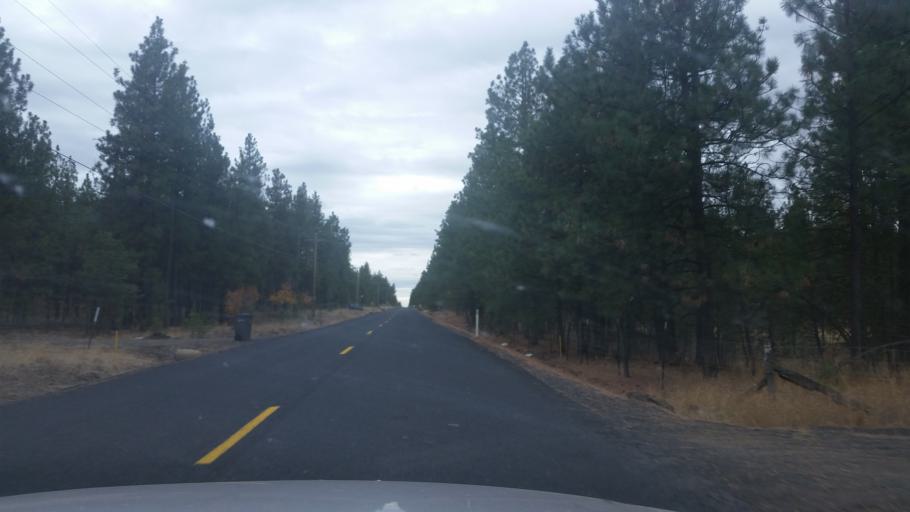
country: US
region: Washington
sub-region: Spokane County
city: Medical Lake
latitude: 47.4787
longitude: -117.7792
